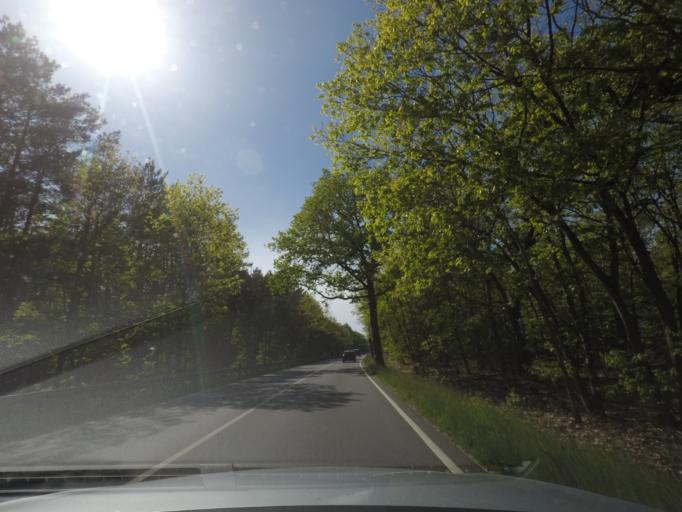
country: DE
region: Brandenburg
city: Luebben
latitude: 51.9454
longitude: 13.8203
